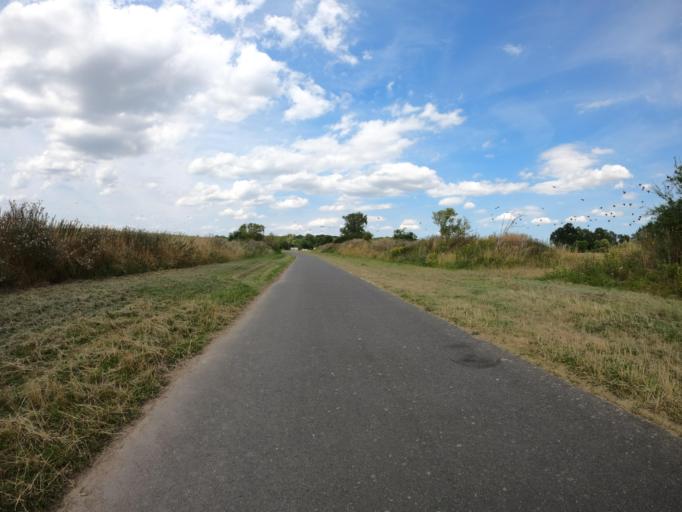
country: DE
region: Mecklenburg-Vorpommern
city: Woldegk
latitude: 53.3516
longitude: 13.5960
